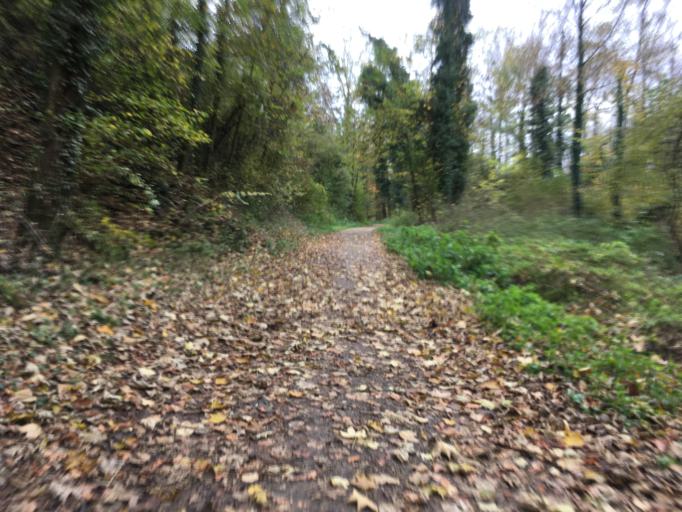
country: DE
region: Baden-Wuerttemberg
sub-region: Freiburg Region
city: Sasbach
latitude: 48.1039
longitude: 7.5893
